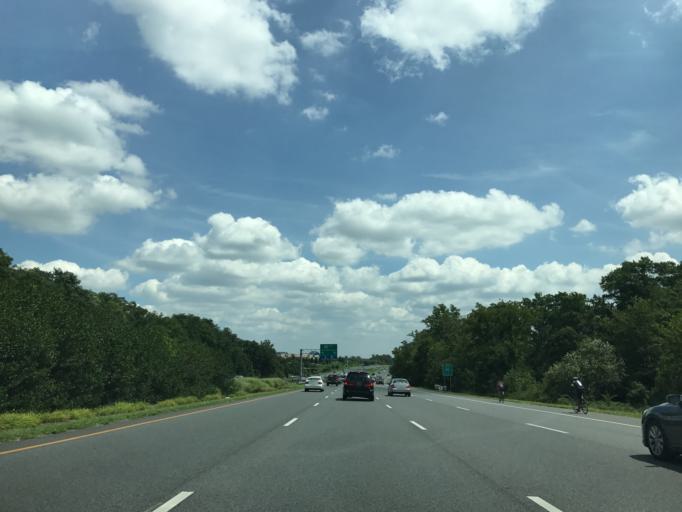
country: US
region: Maryland
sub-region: Anne Arundel County
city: Jessup
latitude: 39.1858
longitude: -76.8027
